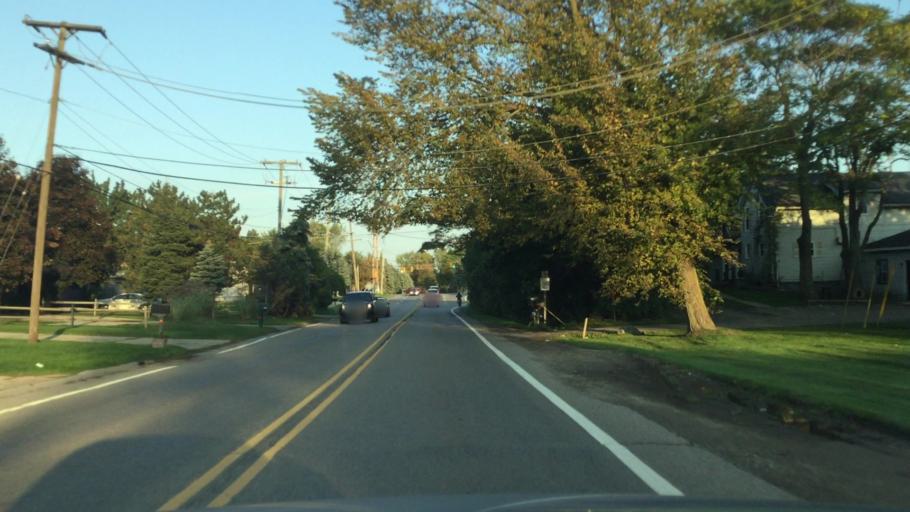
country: US
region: Michigan
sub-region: Oakland County
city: Keego Harbor
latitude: 42.6249
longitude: -83.3574
